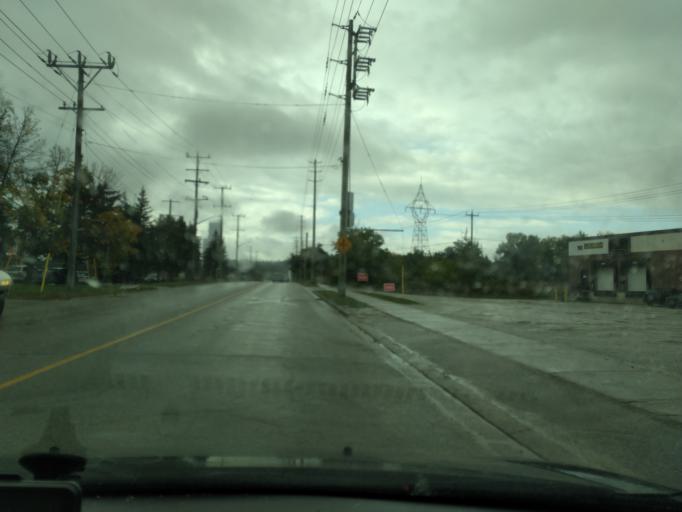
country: CA
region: Ontario
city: Barrie
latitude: 44.3698
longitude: -79.7089
